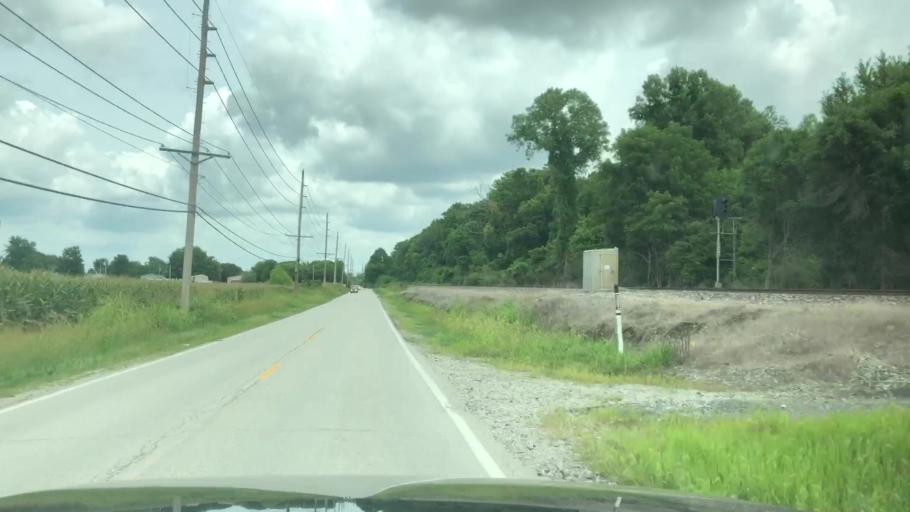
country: US
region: Missouri
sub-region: Saint Charles County
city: Saint Charles
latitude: 38.8142
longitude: -90.5284
